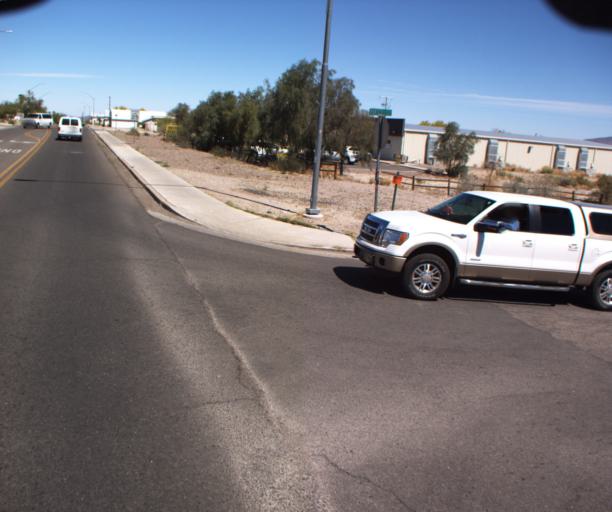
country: US
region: Arizona
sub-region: Pima County
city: Ajo
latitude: 32.3787
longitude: -112.8724
